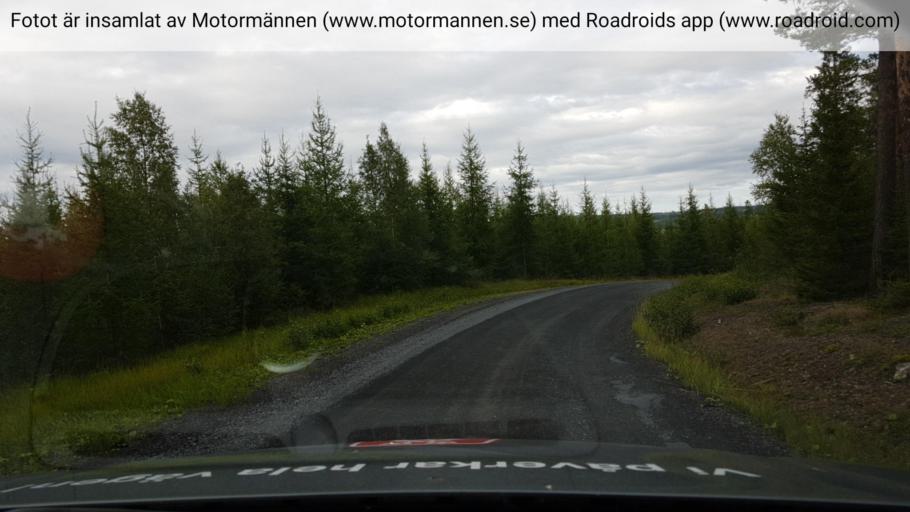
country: SE
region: Jaemtland
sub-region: Krokoms Kommun
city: Valla
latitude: 63.3666
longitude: 13.9118
